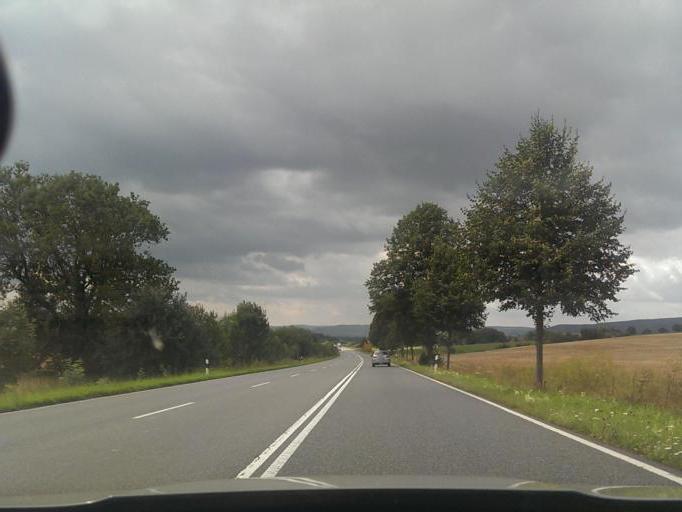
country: DE
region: Lower Saxony
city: Arholzen
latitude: 51.8697
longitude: 9.5385
